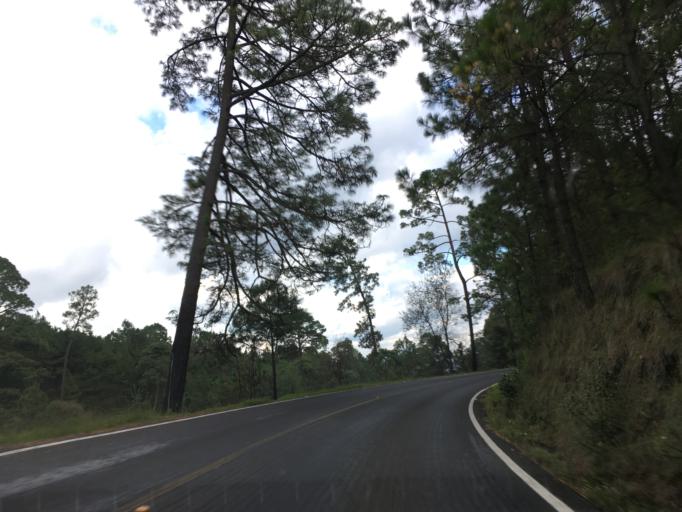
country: MX
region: Michoacan
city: Pichataro
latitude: 19.6000
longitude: -101.8338
